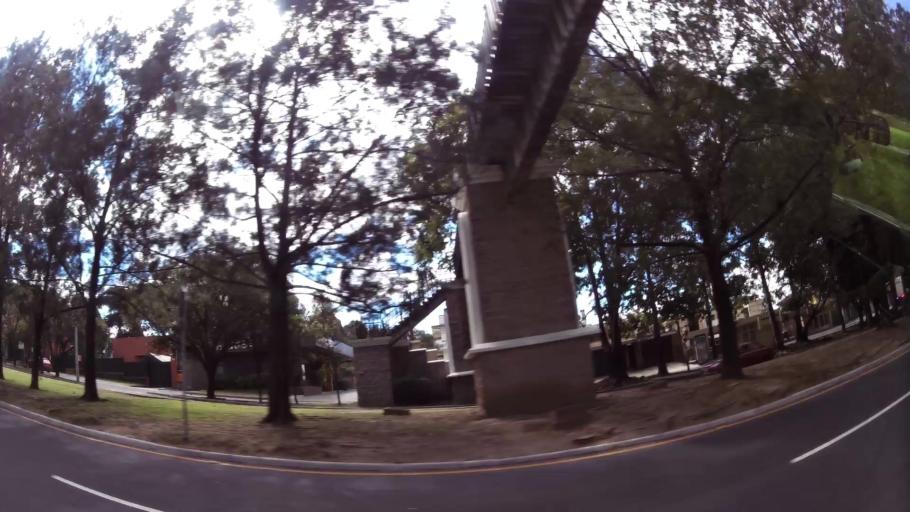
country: GT
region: Guatemala
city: Santa Catarina Pinula
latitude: 14.5828
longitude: -90.4857
